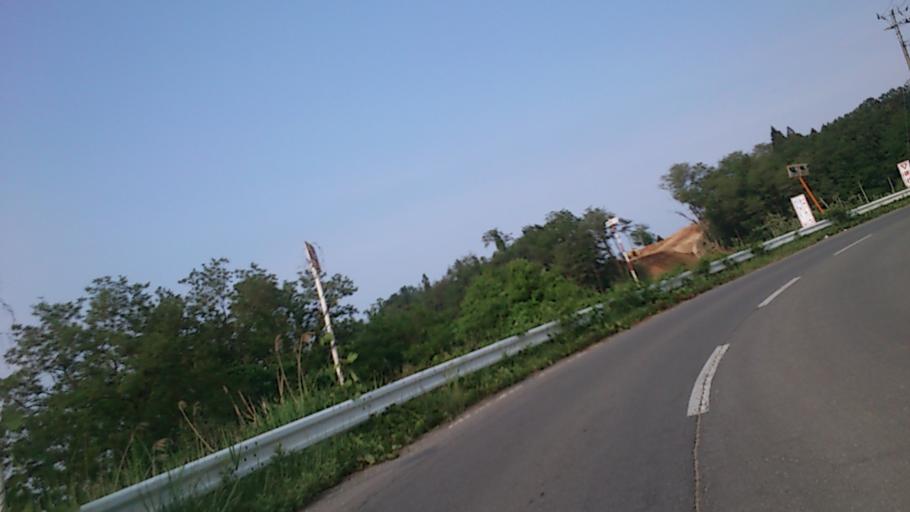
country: JP
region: Aomori
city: Hirosaki
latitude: 40.5557
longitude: 140.4732
